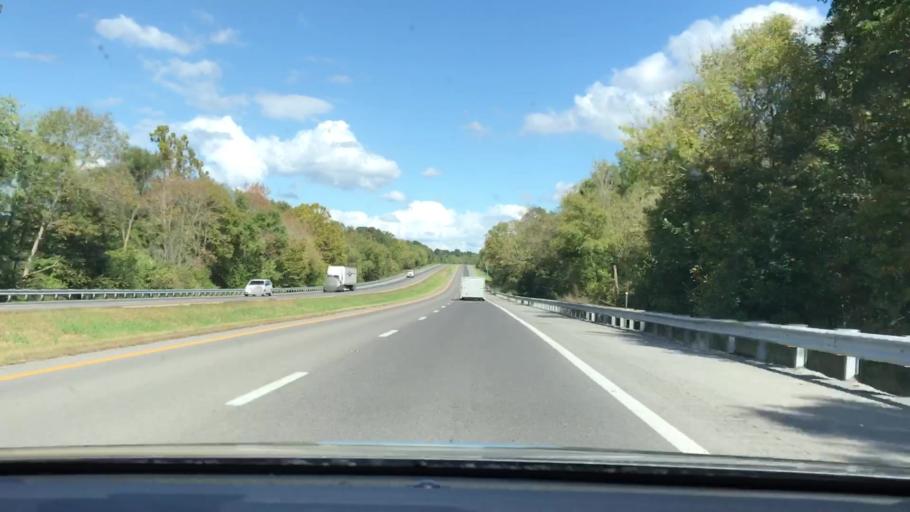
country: US
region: Kentucky
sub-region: Marshall County
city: Benton
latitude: 36.8408
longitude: -88.4171
